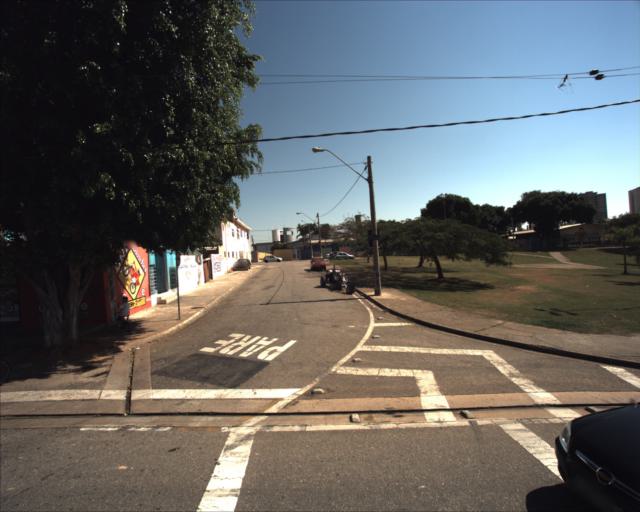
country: BR
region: Sao Paulo
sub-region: Sorocaba
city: Sorocaba
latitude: -23.4999
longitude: -47.5075
